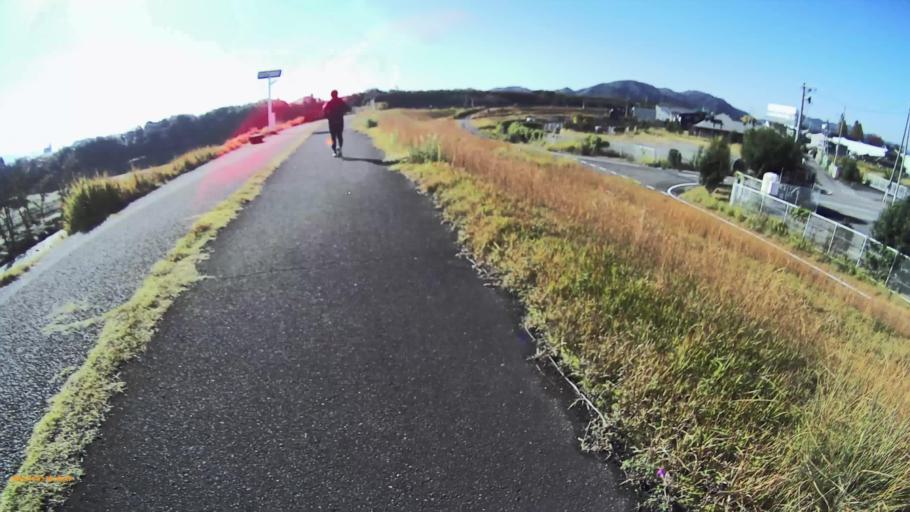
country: JP
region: Gifu
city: Minokamo
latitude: 35.4390
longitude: 137.0311
